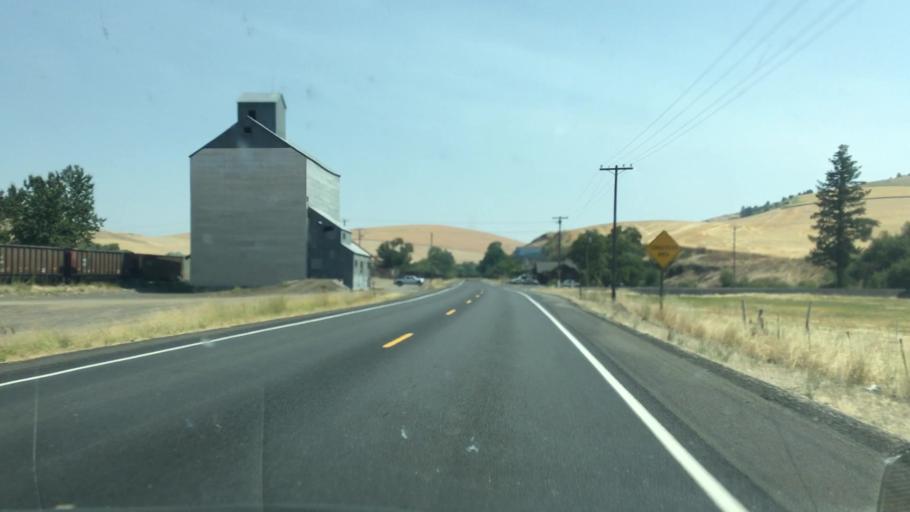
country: US
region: Idaho
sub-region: Nez Perce County
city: Lapwai
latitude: 46.3690
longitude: -116.7272
